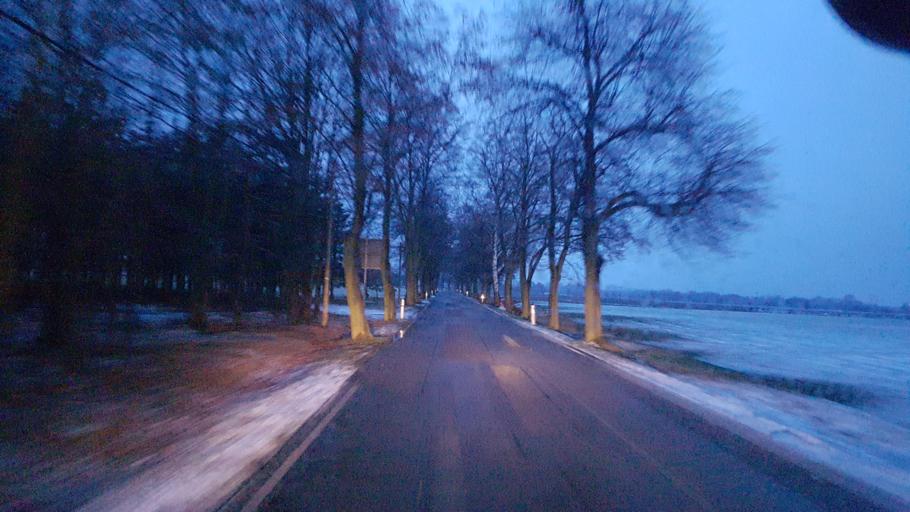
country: DE
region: Brandenburg
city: Guhrow
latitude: 51.8070
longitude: 14.2231
